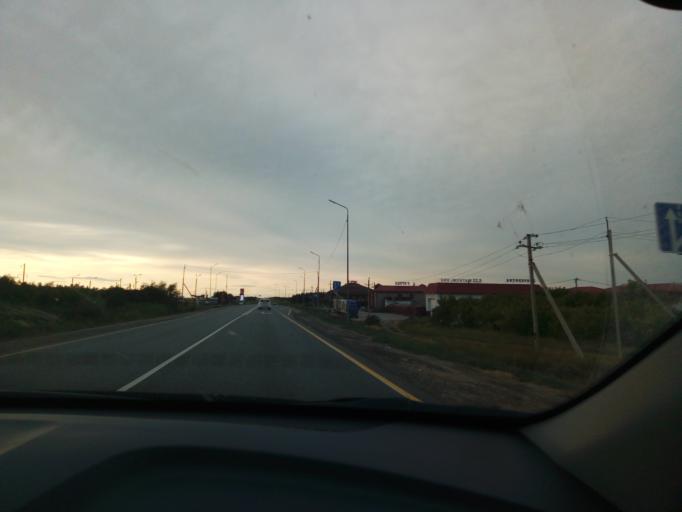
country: RU
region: Volgograd
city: Primorsk
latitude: 49.2645
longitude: 44.8804
